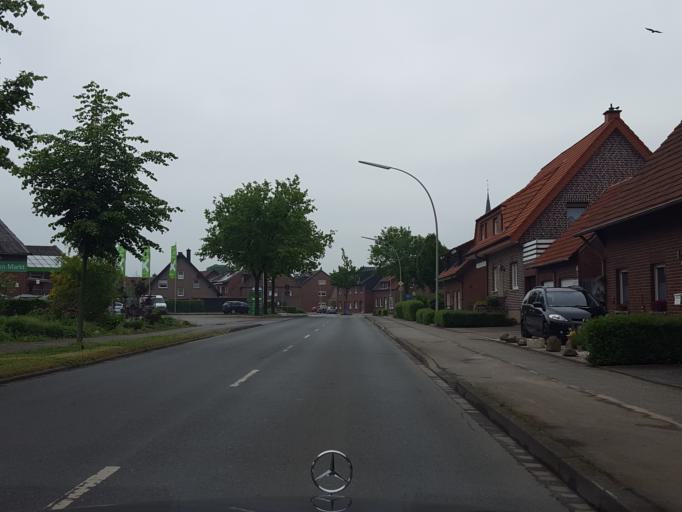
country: DE
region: North Rhine-Westphalia
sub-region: Regierungsbezirk Munster
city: Senden
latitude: 51.8211
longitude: 7.5471
